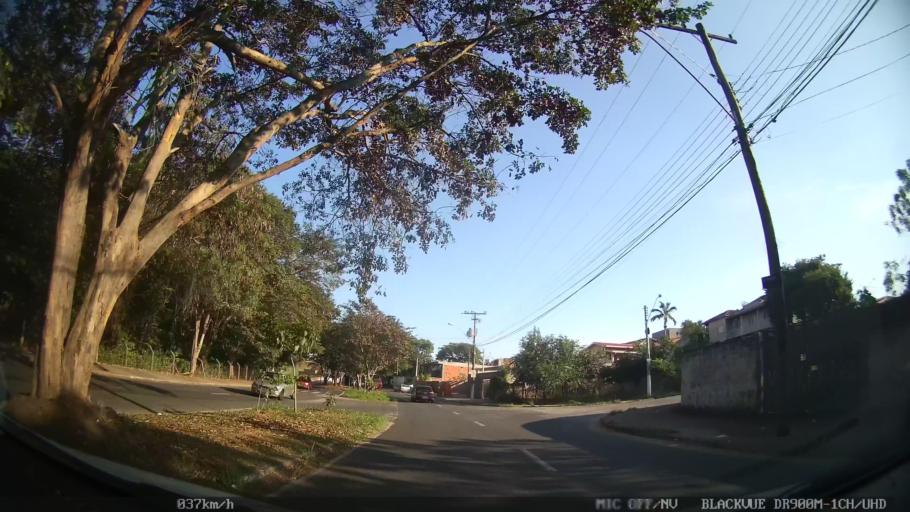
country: BR
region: Sao Paulo
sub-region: Campinas
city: Campinas
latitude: -22.9770
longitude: -47.1454
